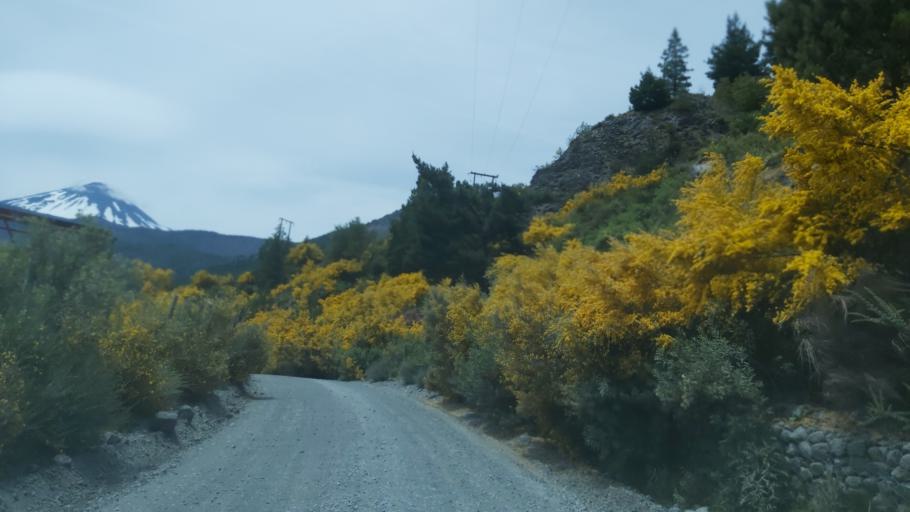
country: AR
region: Neuquen
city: Andacollo
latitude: -37.3977
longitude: -71.4458
